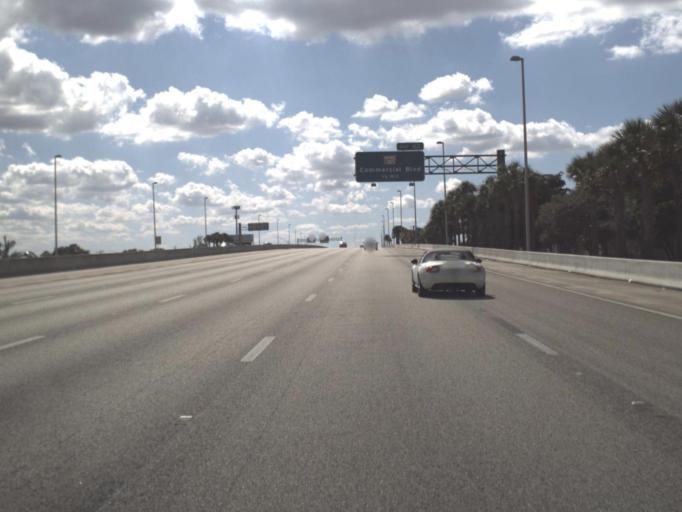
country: US
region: Florida
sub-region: Broward County
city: Palm Aire
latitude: 26.2035
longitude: -80.2013
